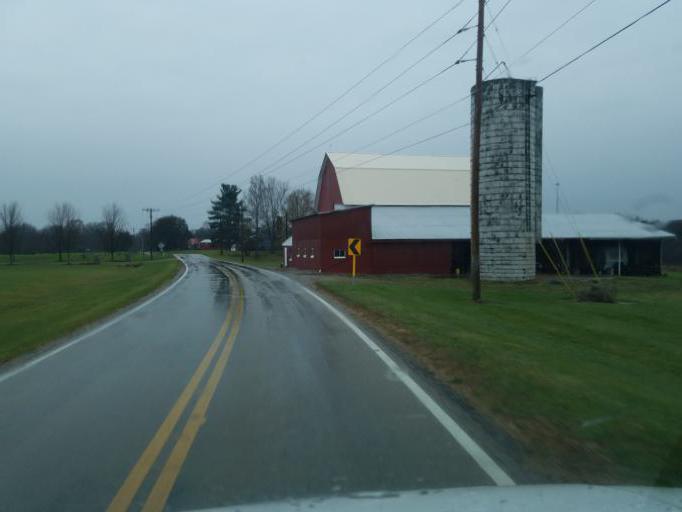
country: US
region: Ohio
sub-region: Delaware County
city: Sunbury
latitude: 40.3029
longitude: -82.8796
